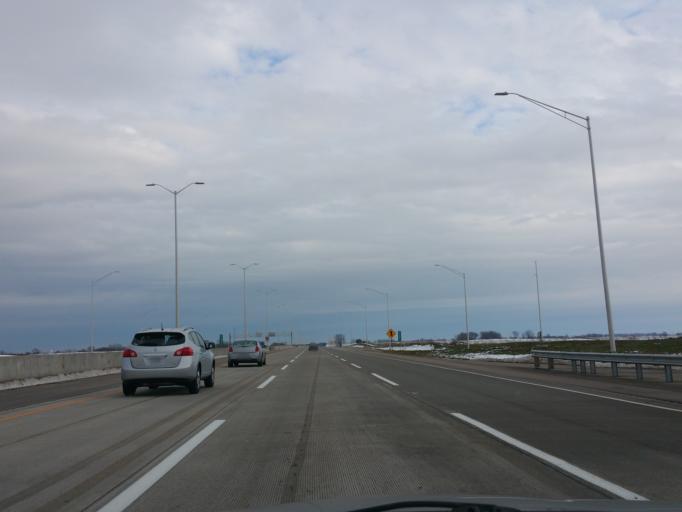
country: US
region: Illinois
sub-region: Winnebago County
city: Cherry Valley
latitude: 42.2330
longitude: -88.8978
